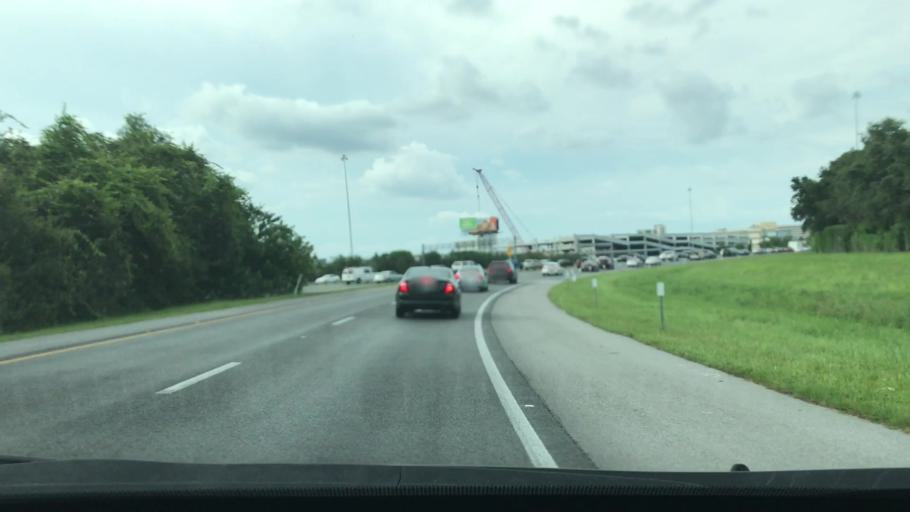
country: US
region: Florida
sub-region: Osceola County
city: Celebration
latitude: 28.3637
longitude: -81.5159
